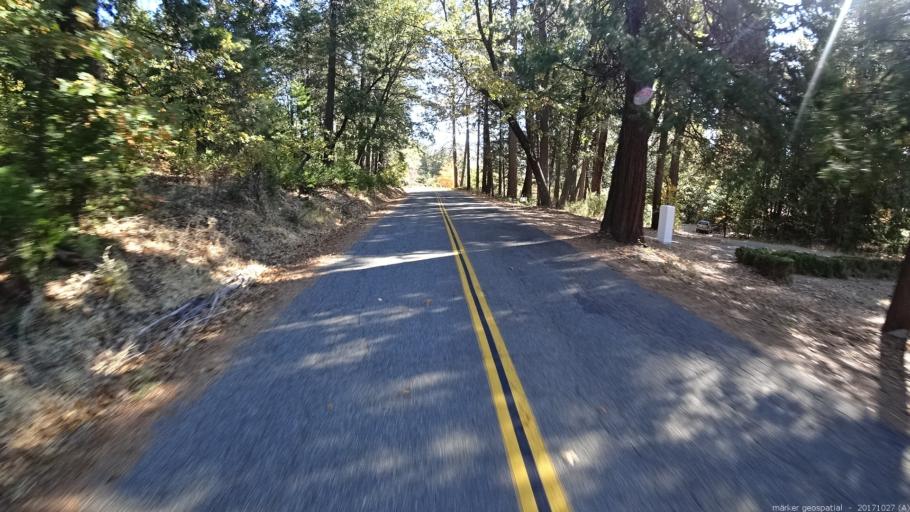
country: US
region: California
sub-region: Shasta County
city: Burney
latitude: 40.8245
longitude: -121.9548
